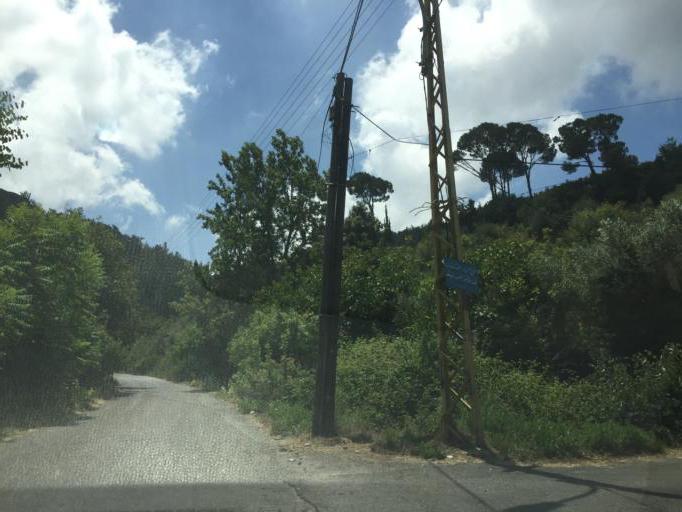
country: LB
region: Mont-Liban
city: Beit ed Dine
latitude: 33.6939
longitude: 35.5736
